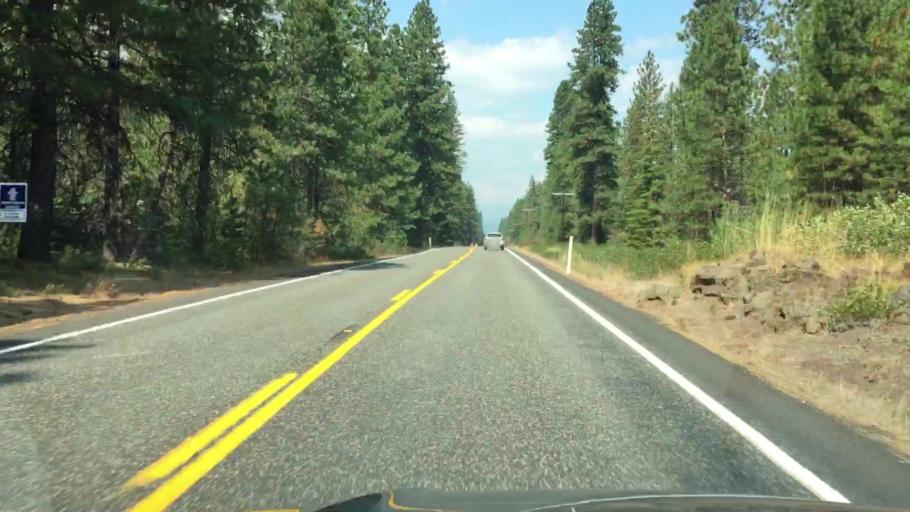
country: US
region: Washington
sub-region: Klickitat County
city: White Salmon
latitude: 45.9792
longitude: -121.5059
